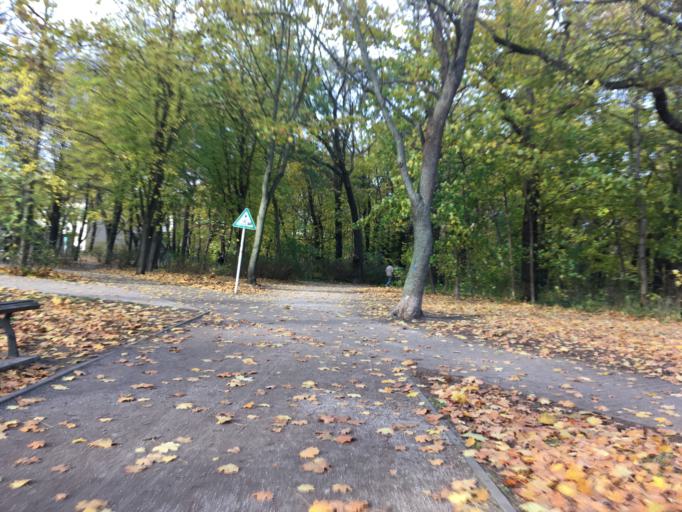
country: DE
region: Berlin
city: Friedrichsfelde
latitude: 52.4963
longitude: 13.5172
